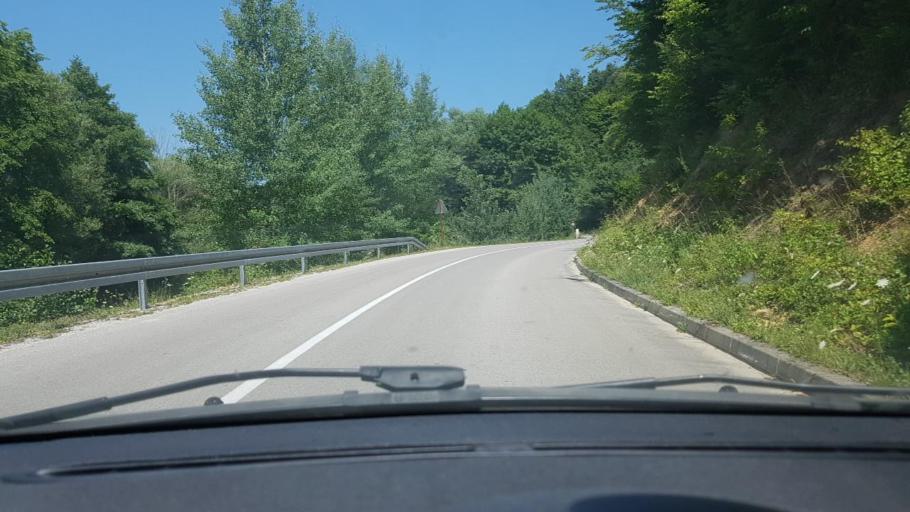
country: BA
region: Federation of Bosnia and Herzegovina
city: Orasac
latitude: 44.5595
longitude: 16.1028
